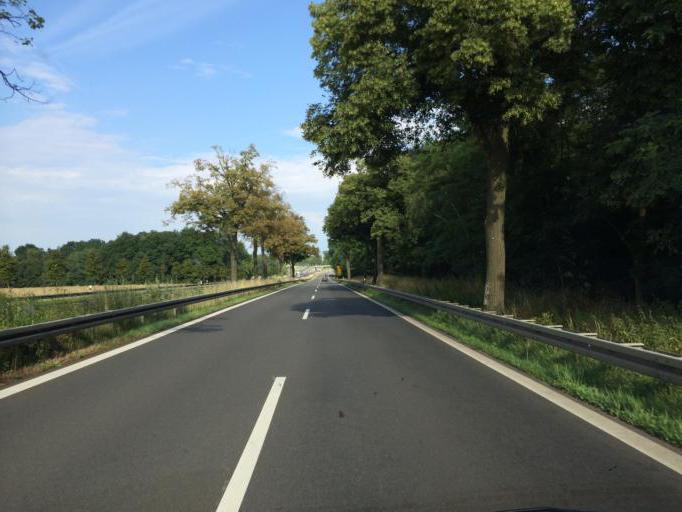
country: DE
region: Brandenburg
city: Dallgow-Doeberitz
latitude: 52.5339
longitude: 13.0343
